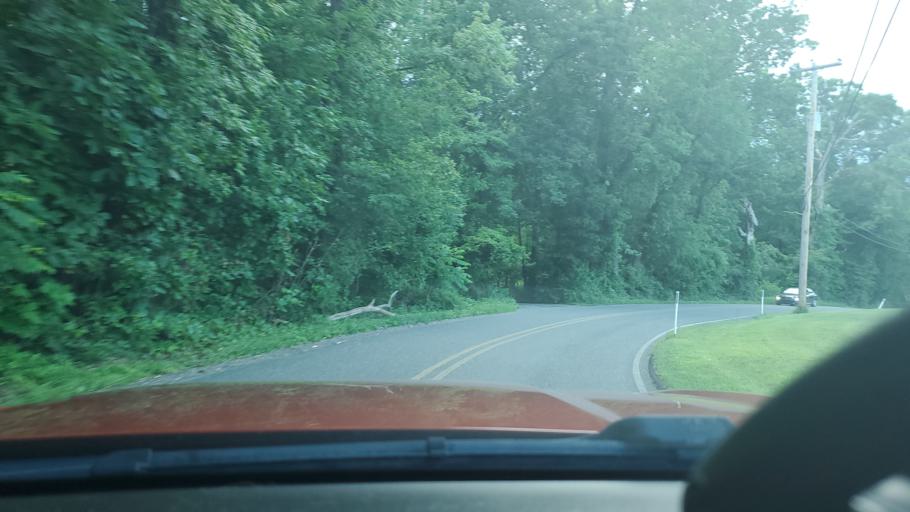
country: US
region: Pennsylvania
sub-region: Montgomery County
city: Limerick
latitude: 40.2425
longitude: -75.5211
